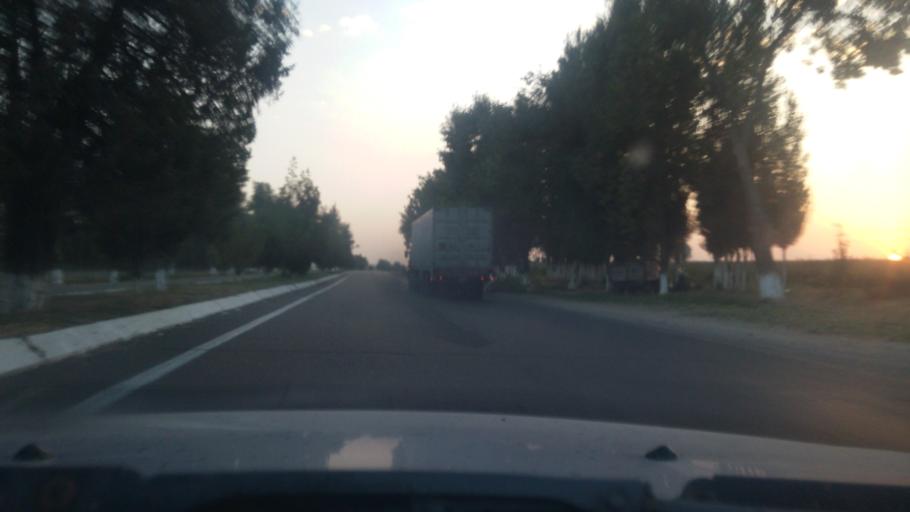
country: UZ
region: Toshkent
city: Zafar
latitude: 41.0012
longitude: 68.8227
